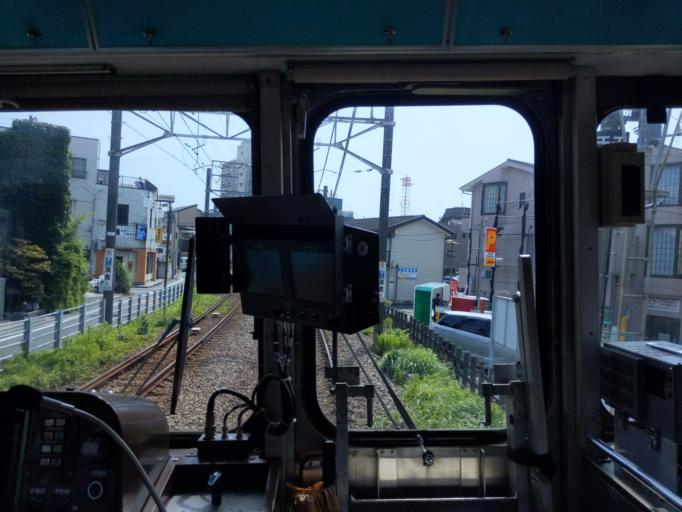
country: JP
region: Kanagawa
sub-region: Kawasaki-shi
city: Kawasaki
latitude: 35.5723
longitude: 139.6924
